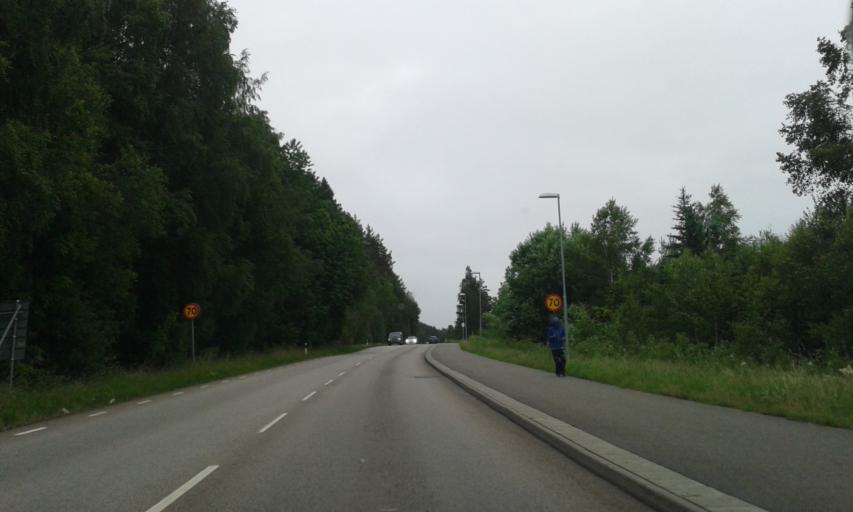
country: SE
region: Vaestra Goetaland
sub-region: Partille Kommun
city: Partille
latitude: 57.7416
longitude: 12.0786
